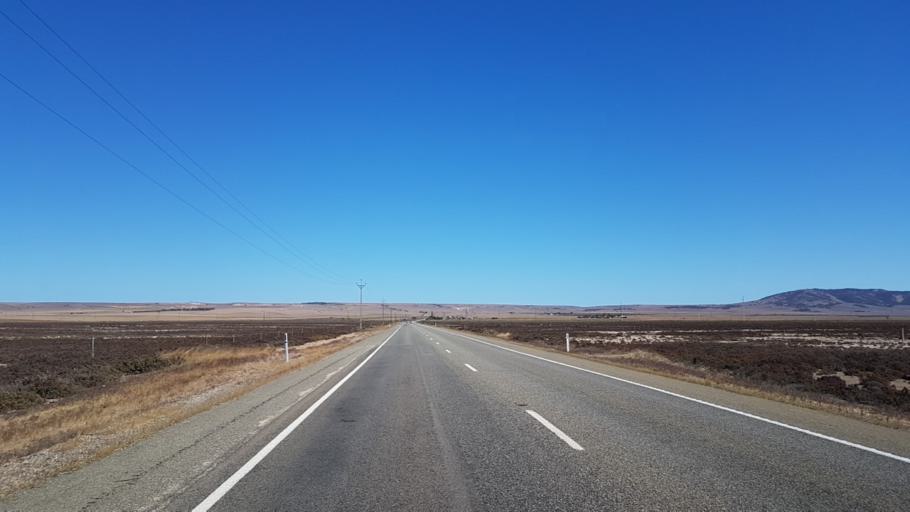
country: AU
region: South Australia
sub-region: Wakefield
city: Balaklava
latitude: -34.0986
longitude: 138.1035
